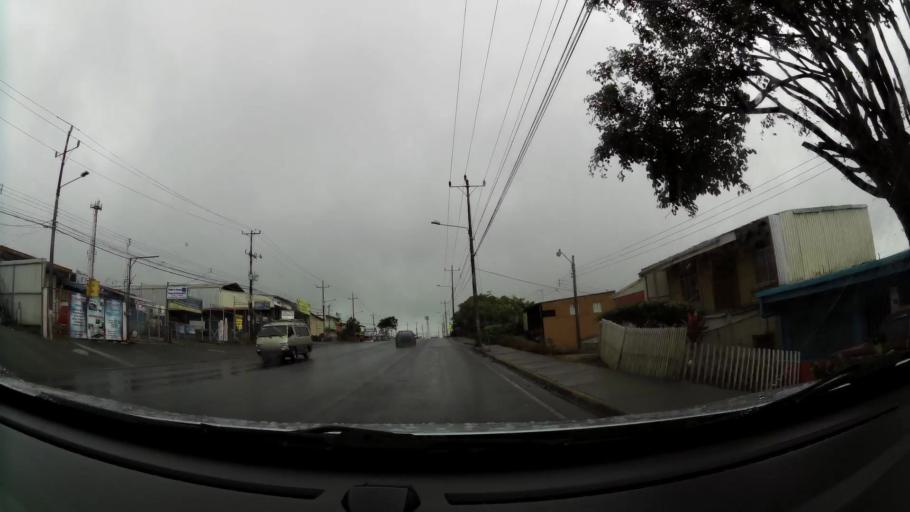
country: CR
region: Cartago
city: Paraiso
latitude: 9.8430
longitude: -83.8829
